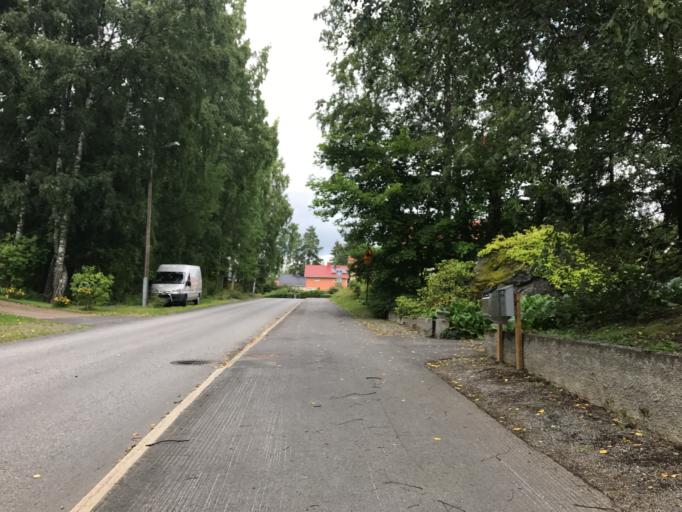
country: FI
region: Pirkanmaa
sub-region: Etelae-Pirkanmaa
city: Valkeakoski
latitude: 61.2586
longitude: 24.0436
